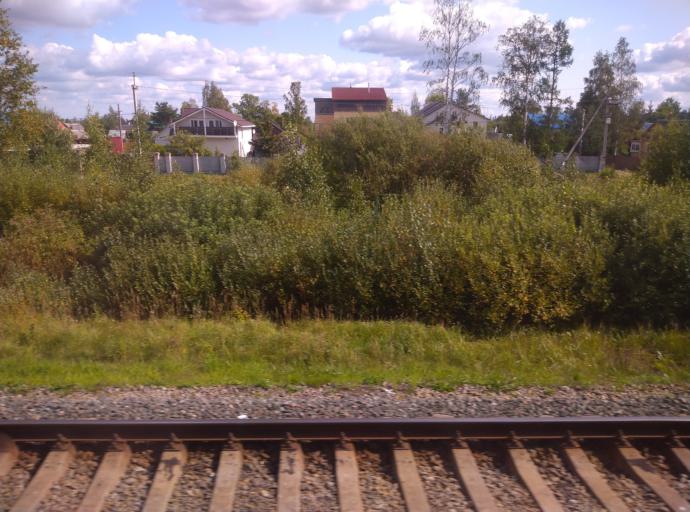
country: RU
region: Leningrad
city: Ul'yanovka
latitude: 59.6300
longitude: 30.7642
